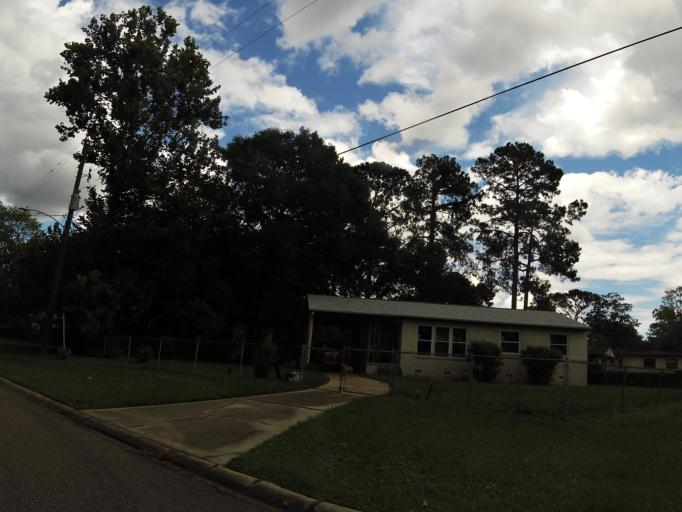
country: US
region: Florida
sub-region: Duval County
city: Jacksonville
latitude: 30.4224
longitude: -81.6702
